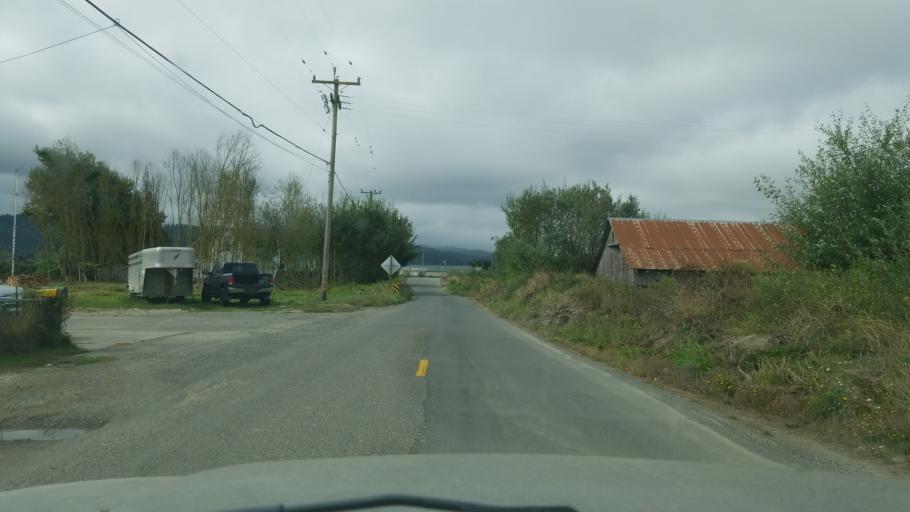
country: US
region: California
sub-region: Humboldt County
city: Ferndale
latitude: 40.5943
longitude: -124.2565
